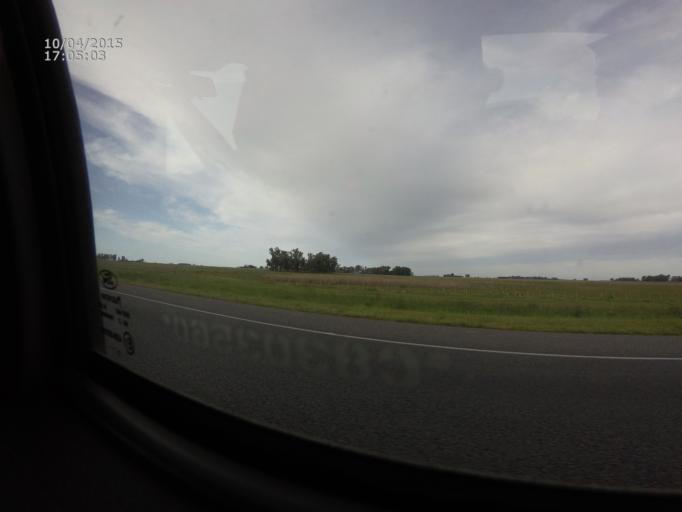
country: AR
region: Buenos Aires
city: Coronel Vidal
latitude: -37.3905
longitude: -57.7454
